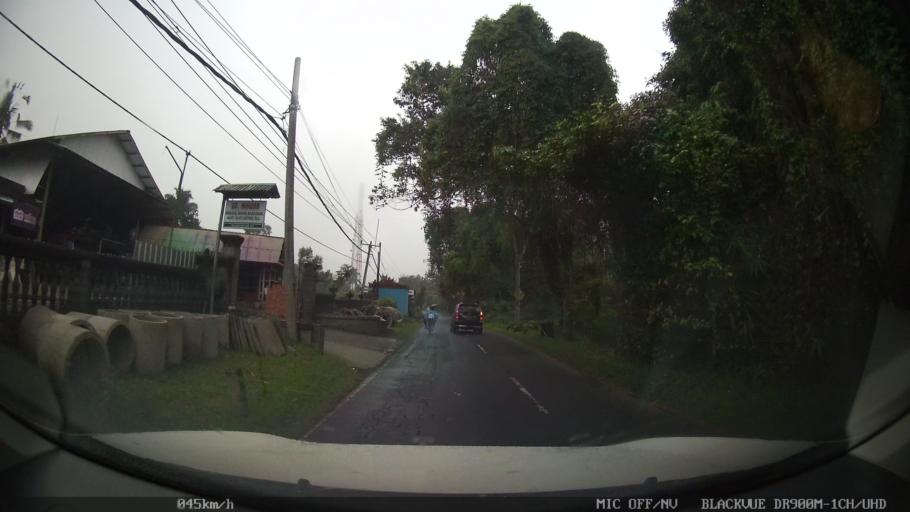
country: ID
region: Bali
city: Banjar Taro Kelod
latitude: -8.3593
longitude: 115.2735
